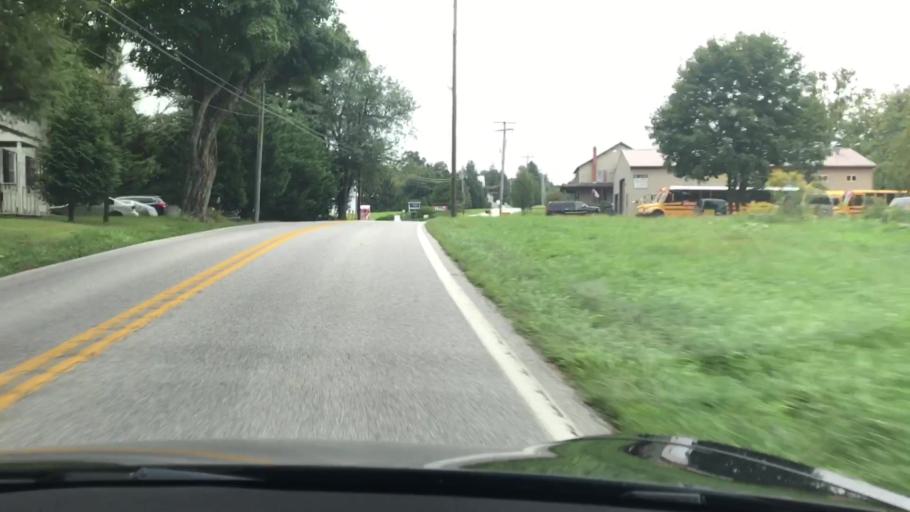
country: US
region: Pennsylvania
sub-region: York County
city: Dillsburg
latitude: 40.1430
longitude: -76.9649
